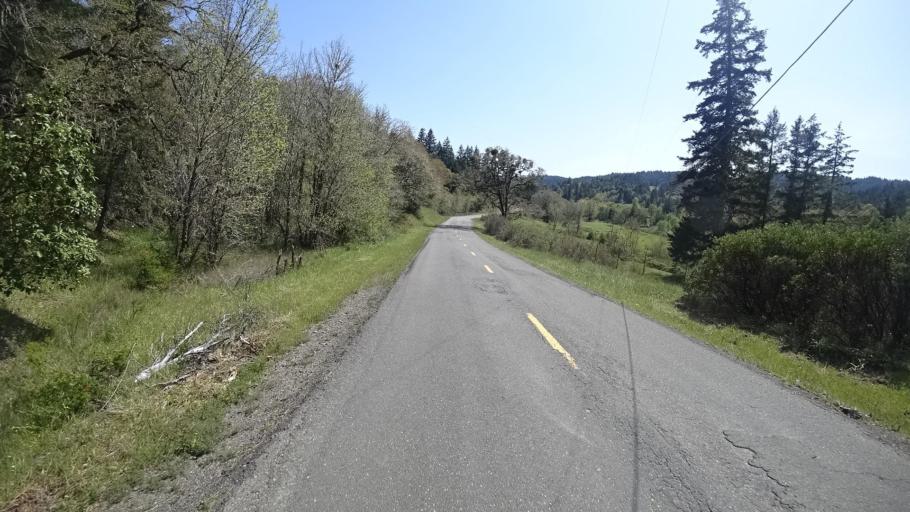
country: US
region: California
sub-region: Humboldt County
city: Redway
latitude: 40.3041
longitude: -123.6544
